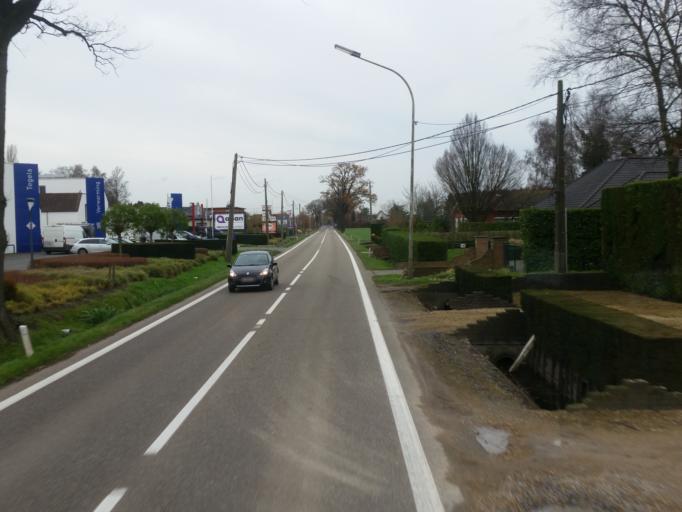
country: BE
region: Flanders
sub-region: Provincie Antwerpen
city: Kalmthout
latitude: 51.3680
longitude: 4.5068
